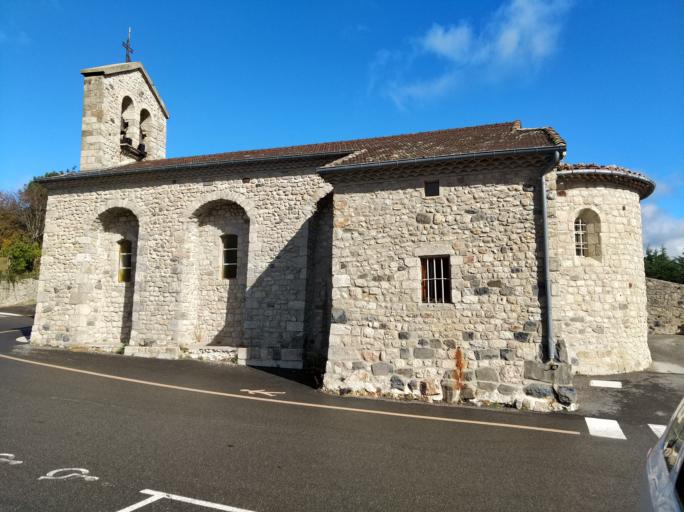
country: FR
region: Rhone-Alpes
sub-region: Departement de l'Ardeche
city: Le Cheylard
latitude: 44.9019
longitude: 4.4608
